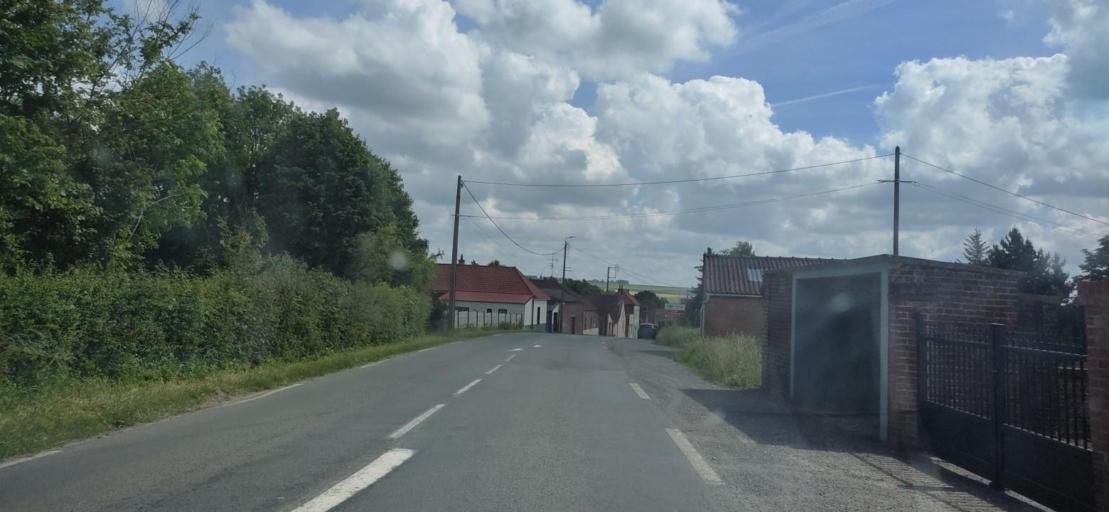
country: FR
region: Nord-Pas-de-Calais
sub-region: Departement du Pas-de-Calais
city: Therouanne
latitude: 50.6425
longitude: 2.2573
